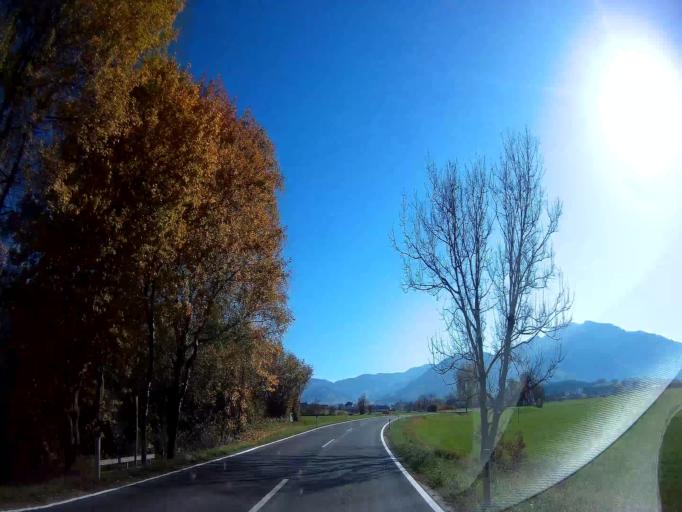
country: AT
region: Salzburg
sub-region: Politischer Bezirk Zell am See
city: Saalfelden am Steinernen Meer
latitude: 47.4360
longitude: 12.8252
